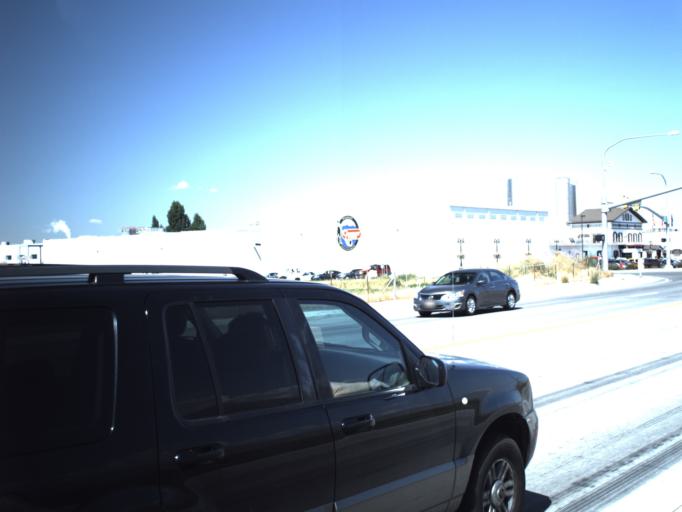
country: US
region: Utah
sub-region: Cache County
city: Logan
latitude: 41.7498
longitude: -111.8590
